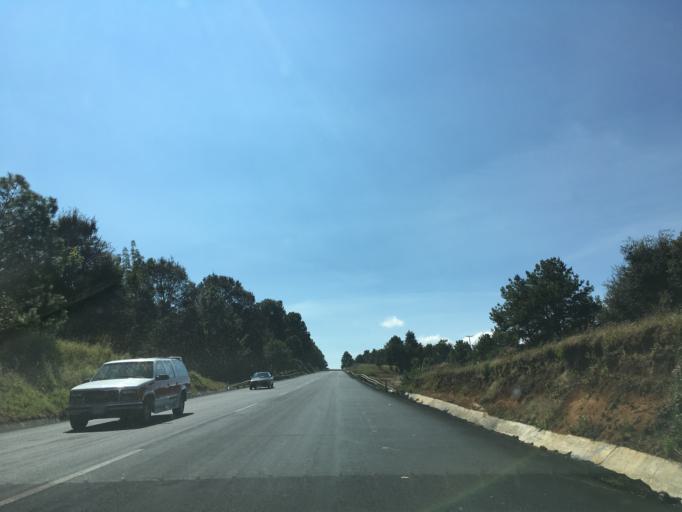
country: MX
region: Michoacan
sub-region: Patzcuaro
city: Santa Ana Chapitiro
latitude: 19.5012
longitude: -101.6942
